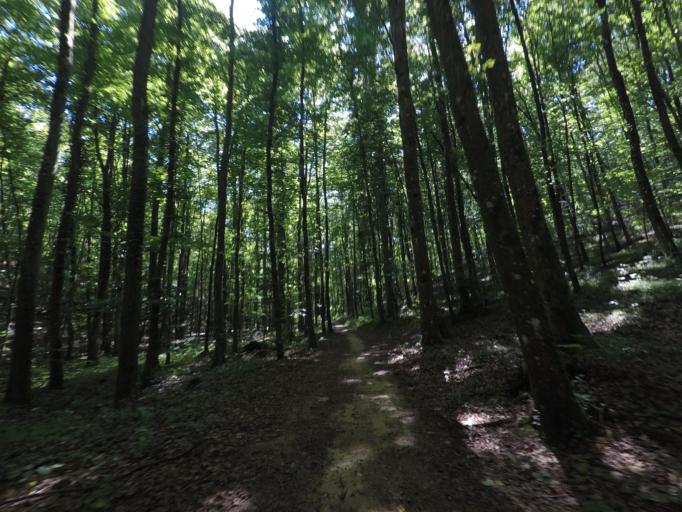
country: LU
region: Luxembourg
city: Bereldange
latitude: 49.6376
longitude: 6.1161
